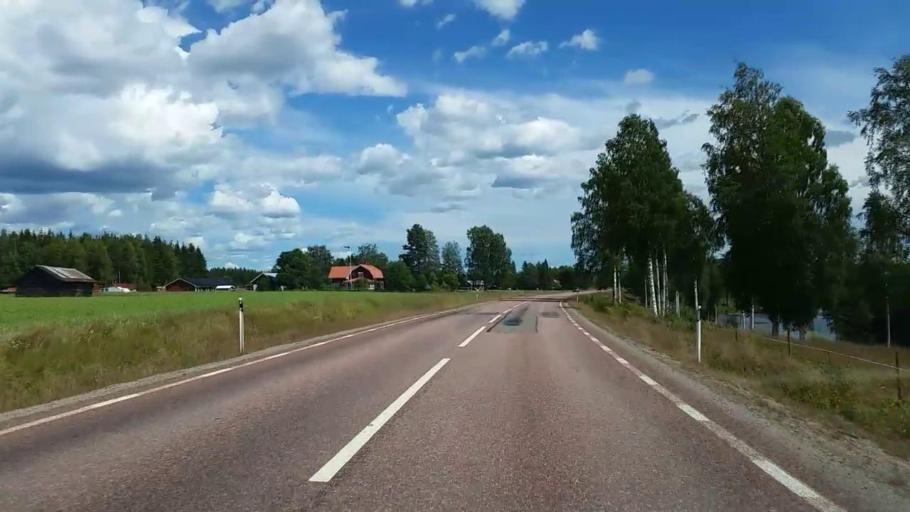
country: SE
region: Gaevleborg
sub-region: Ovanakers Kommun
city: Edsbyn
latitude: 61.3471
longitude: 15.6045
